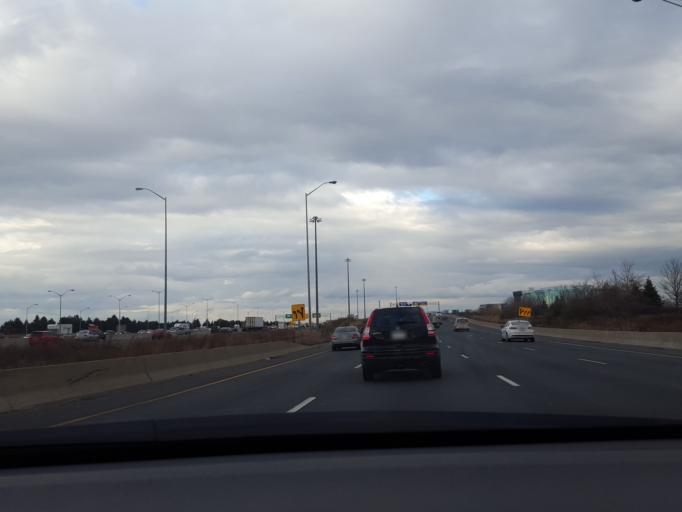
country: CA
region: Ontario
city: Etobicoke
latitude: 43.6542
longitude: -79.6227
